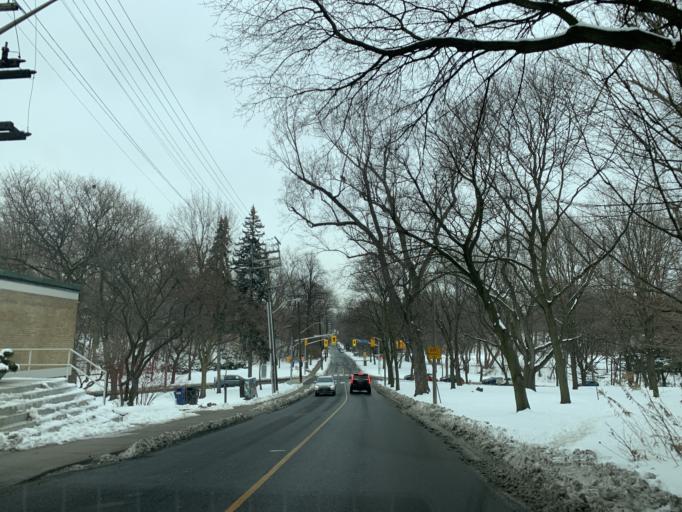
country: CA
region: Ontario
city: Toronto
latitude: 43.6728
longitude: -79.3846
